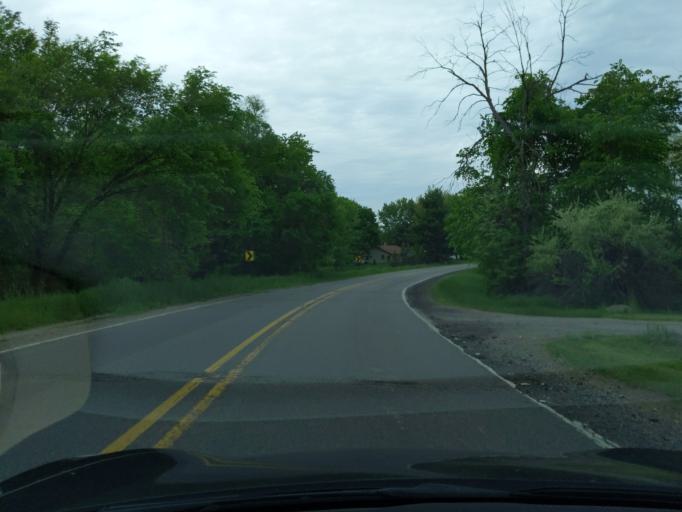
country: US
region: Michigan
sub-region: Ingham County
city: Mason
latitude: 42.6187
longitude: -84.3636
